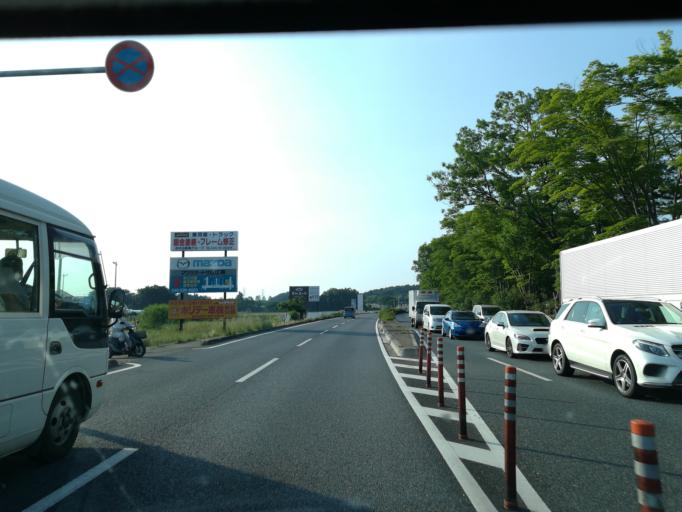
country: JP
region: Saitama
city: Kumagaya
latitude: 36.0613
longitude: 139.3688
